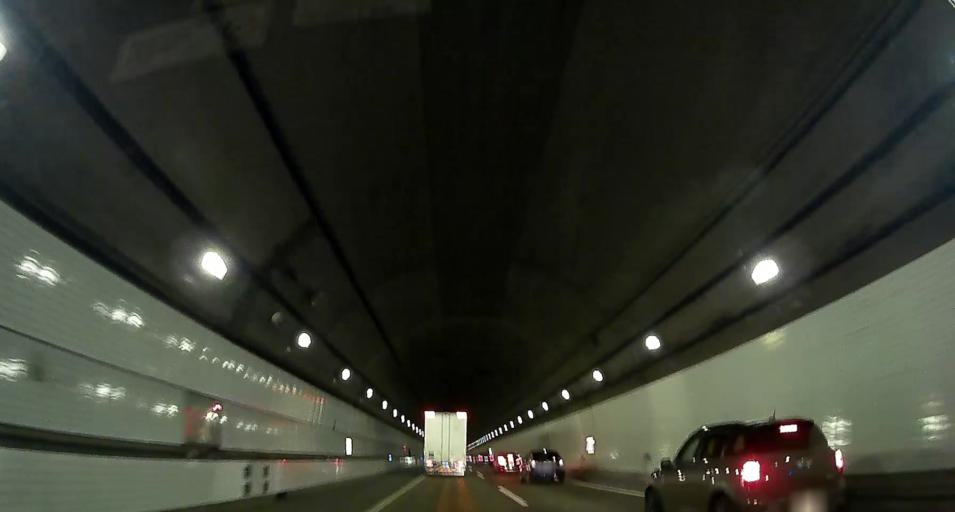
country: JP
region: Chiba
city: Kisarazu
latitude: 35.4713
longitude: 139.8636
